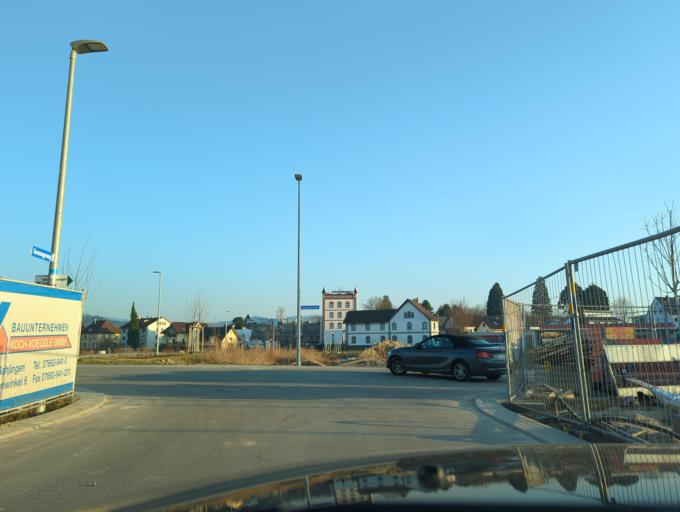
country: DE
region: Baden-Wuerttemberg
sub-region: Freiburg Region
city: Achern
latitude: 48.6300
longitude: 8.0645
